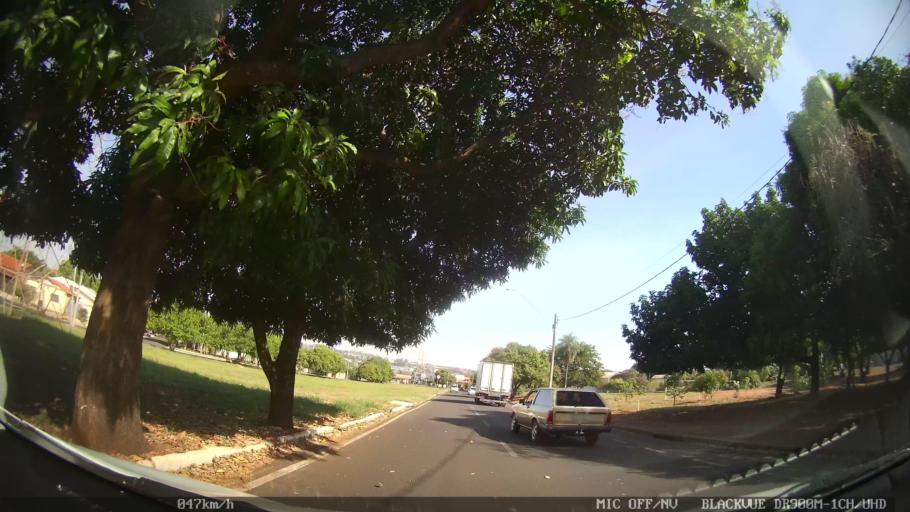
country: BR
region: Sao Paulo
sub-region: Sao Jose Do Rio Preto
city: Sao Jose do Rio Preto
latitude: -20.7961
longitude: -49.4169
